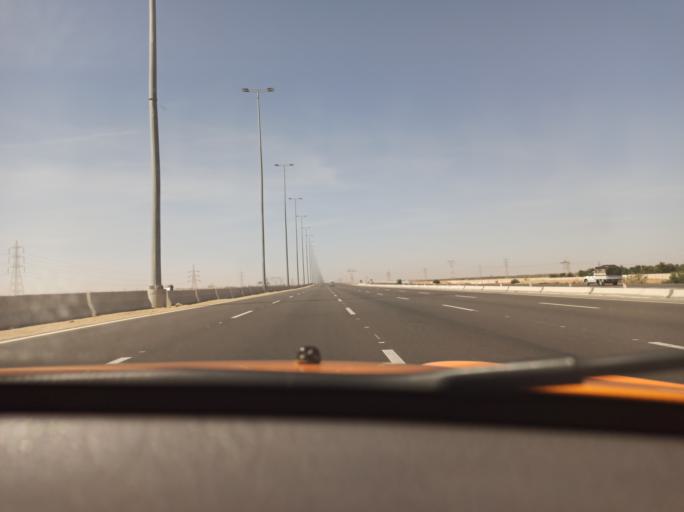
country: EG
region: Al Isma'iliyah
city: At Tall al Kabir
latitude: 30.3332
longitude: 31.8547
